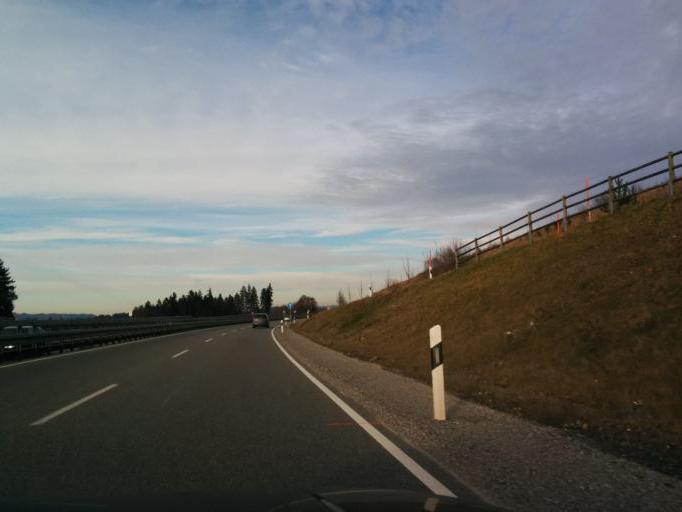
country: DE
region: Bavaria
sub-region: Swabia
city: Waltenhofen
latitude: 47.6397
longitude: 10.2870
